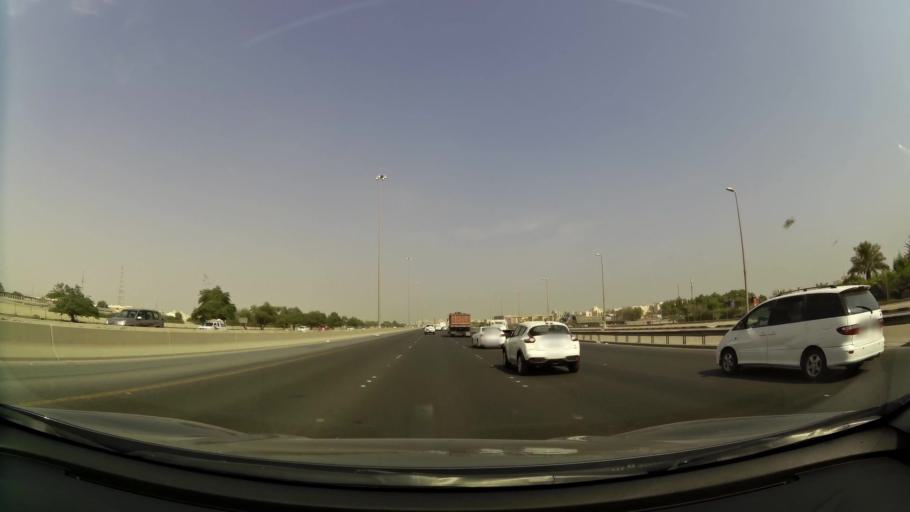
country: KW
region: Al Ahmadi
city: Al Fahahil
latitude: 29.0786
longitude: 48.1133
